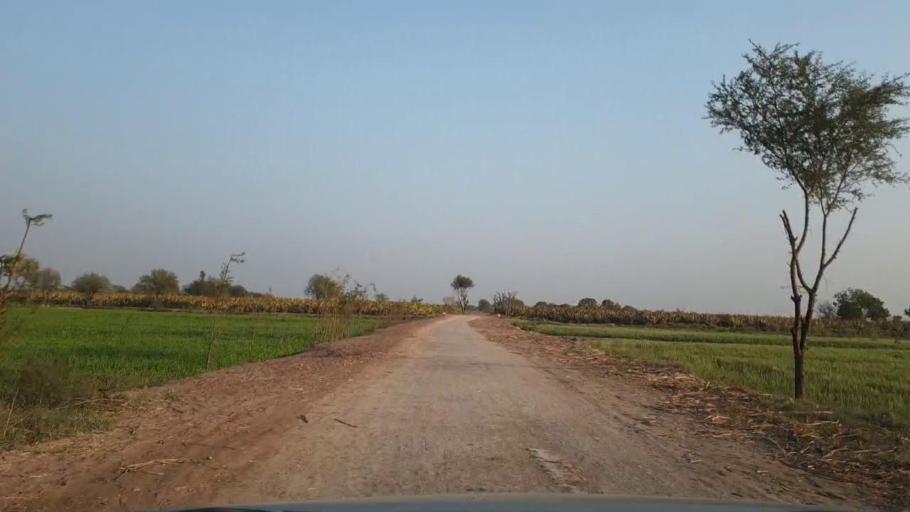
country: PK
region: Sindh
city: Tando Adam
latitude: 25.7122
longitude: 68.5987
